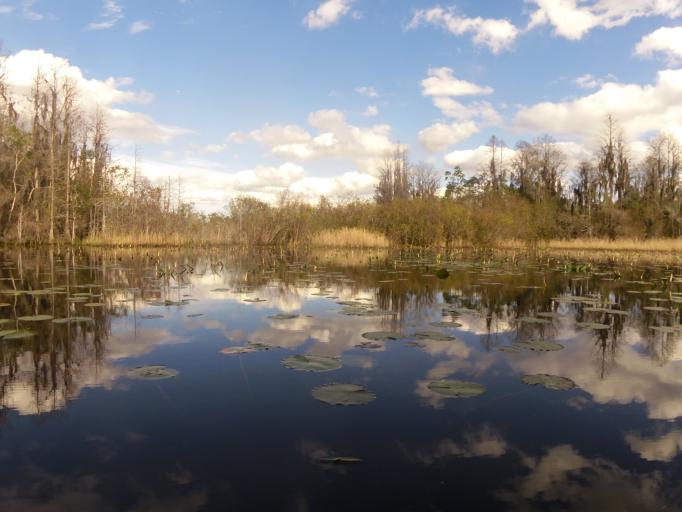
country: US
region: Georgia
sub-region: Charlton County
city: Folkston
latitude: 30.7336
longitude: -82.1746
